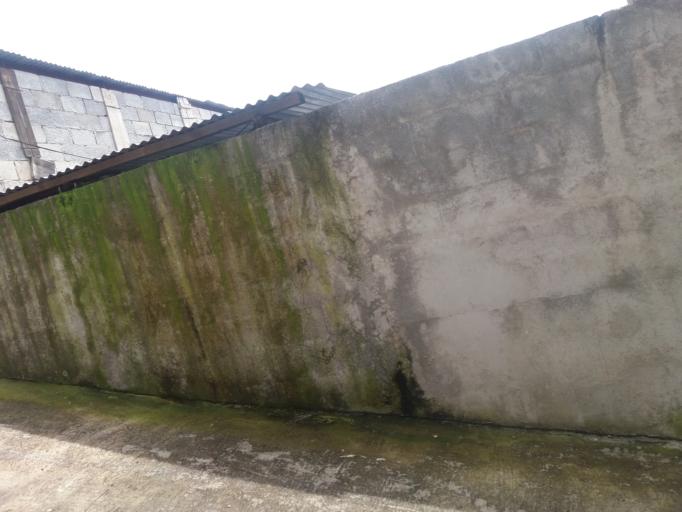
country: GT
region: Guatemala
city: Petapa
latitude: 14.5377
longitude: -90.5266
